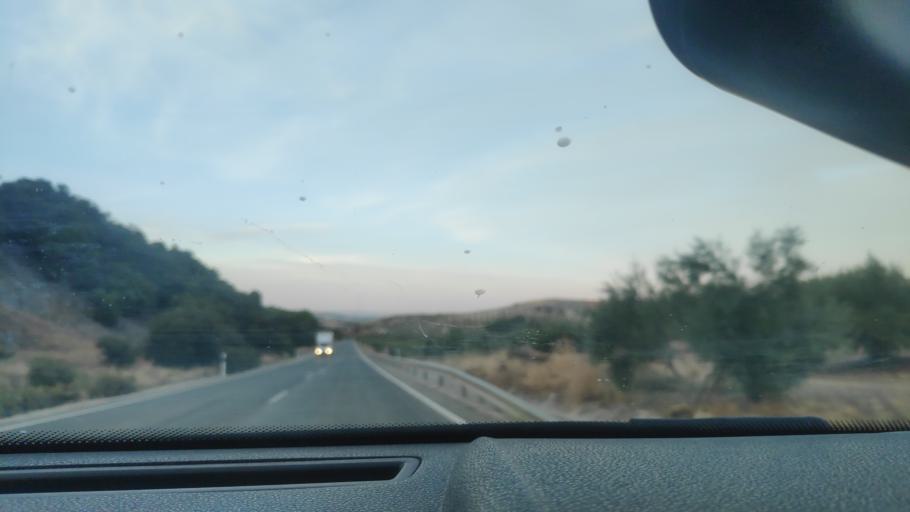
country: ES
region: Andalusia
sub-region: Provincia de Jaen
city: Escanuela
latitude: 37.8342
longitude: -4.0481
